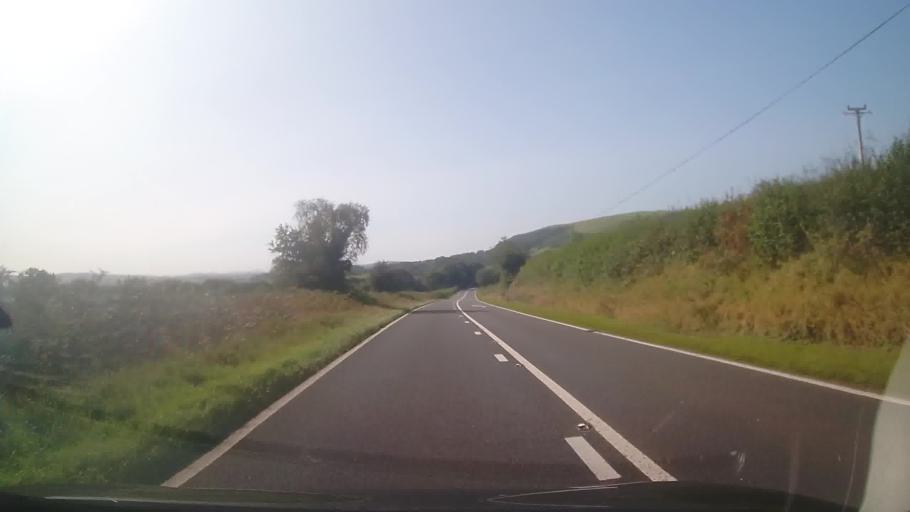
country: GB
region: Wales
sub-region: Sir Powys
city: Rhayader
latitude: 52.1362
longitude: -3.6056
